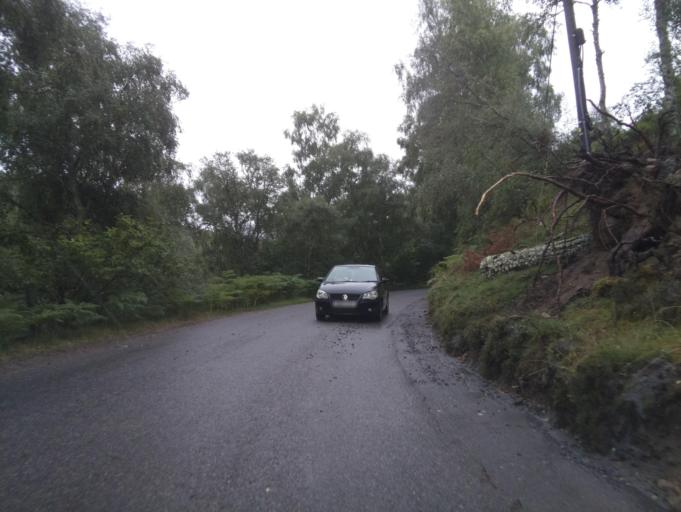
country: GB
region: Scotland
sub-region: Aberdeenshire
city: Ballater
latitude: 57.0790
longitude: -3.0872
